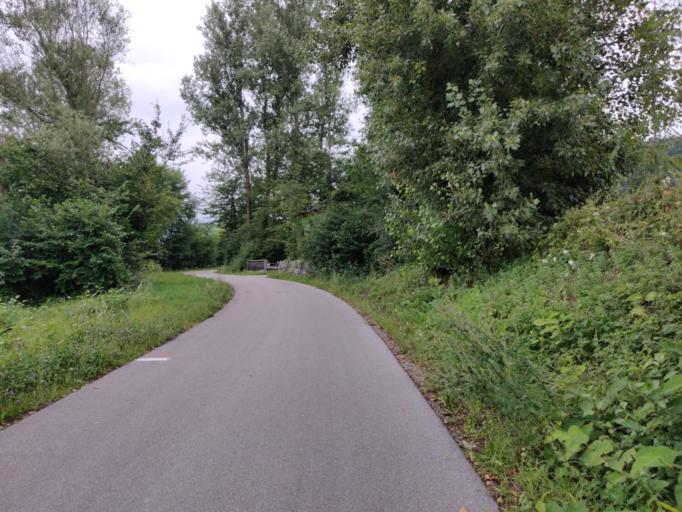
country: AT
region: Lower Austria
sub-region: Politischer Bezirk Melk
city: Ybbs an der Donau
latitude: 48.1796
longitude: 15.1211
